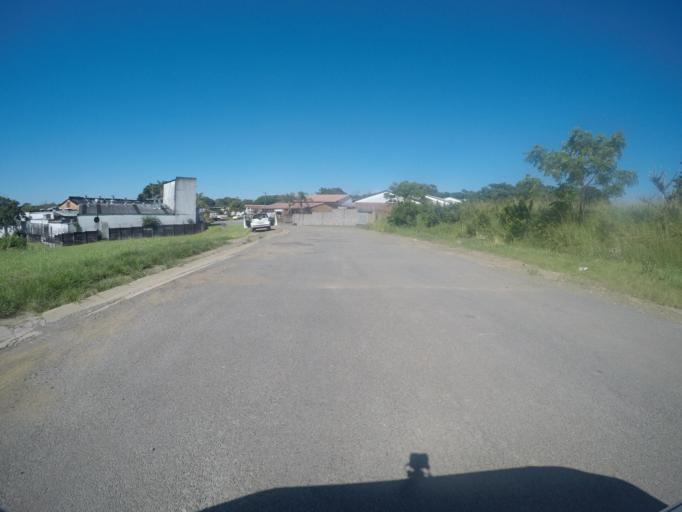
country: ZA
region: Eastern Cape
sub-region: Buffalo City Metropolitan Municipality
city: East London
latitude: -32.9390
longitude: 28.0024
